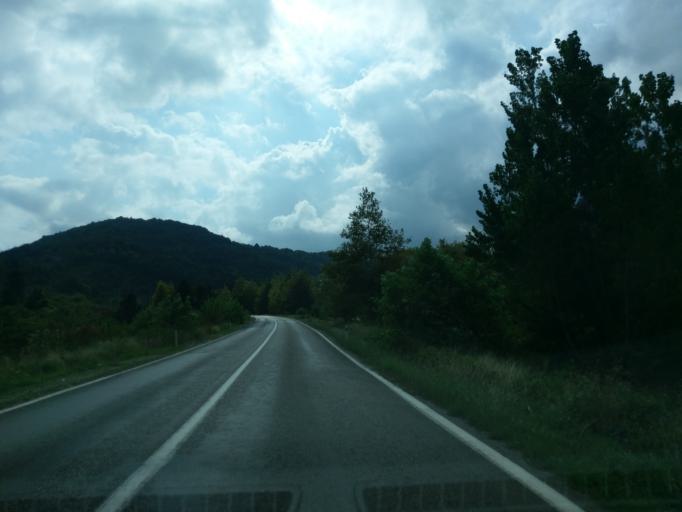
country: TR
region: Sinop
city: Yenikonak
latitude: 41.9403
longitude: 34.7199
